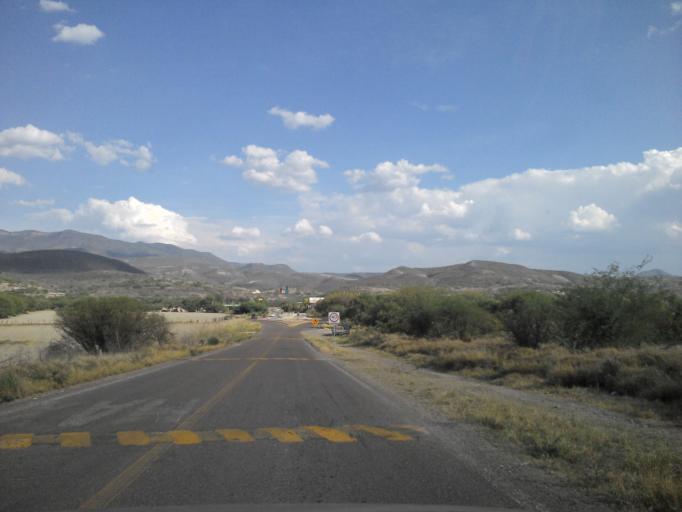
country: MX
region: Zacatecas
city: Juchipila
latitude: 21.2665
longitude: -103.1626
